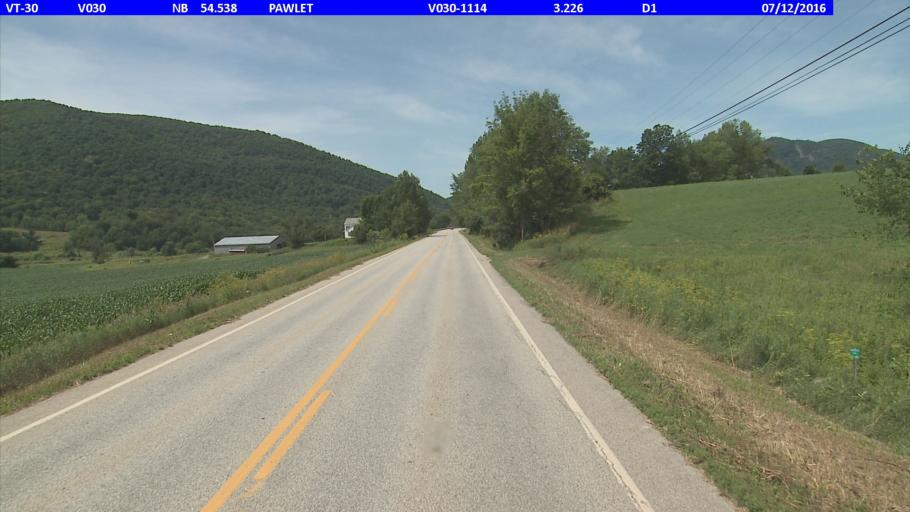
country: US
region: New York
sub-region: Washington County
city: Granville
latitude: 43.3539
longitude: -73.1825
